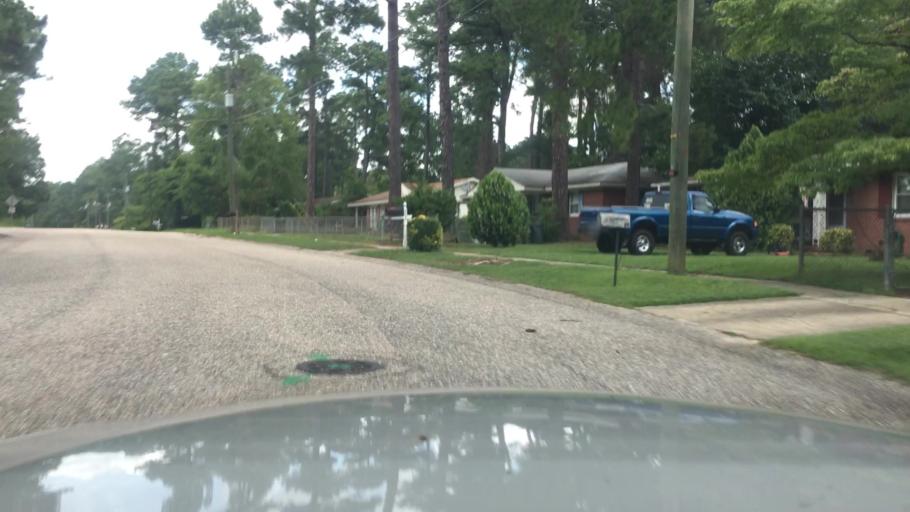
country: US
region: North Carolina
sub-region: Cumberland County
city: Fayetteville
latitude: 35.0488
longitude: -78.9528
